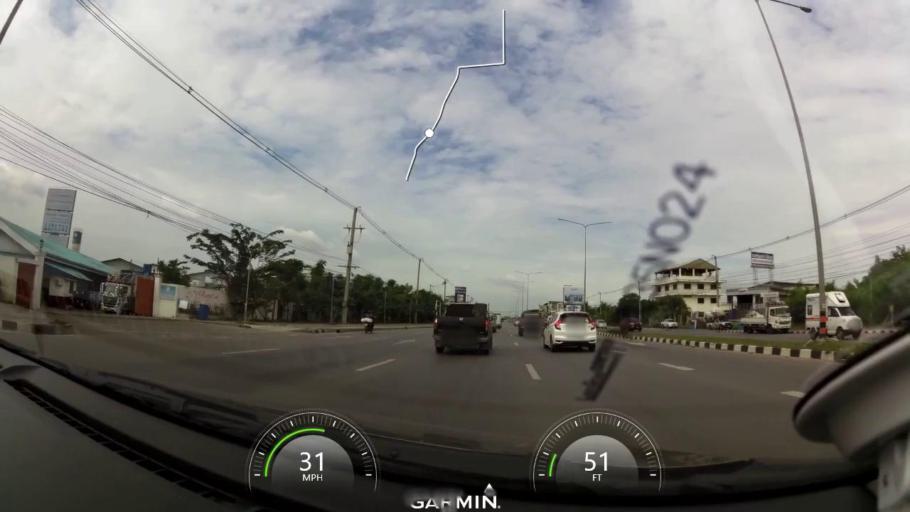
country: TH
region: Samut Sakhon
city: Krathum Baen
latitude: 13.6579
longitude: 100.3107
